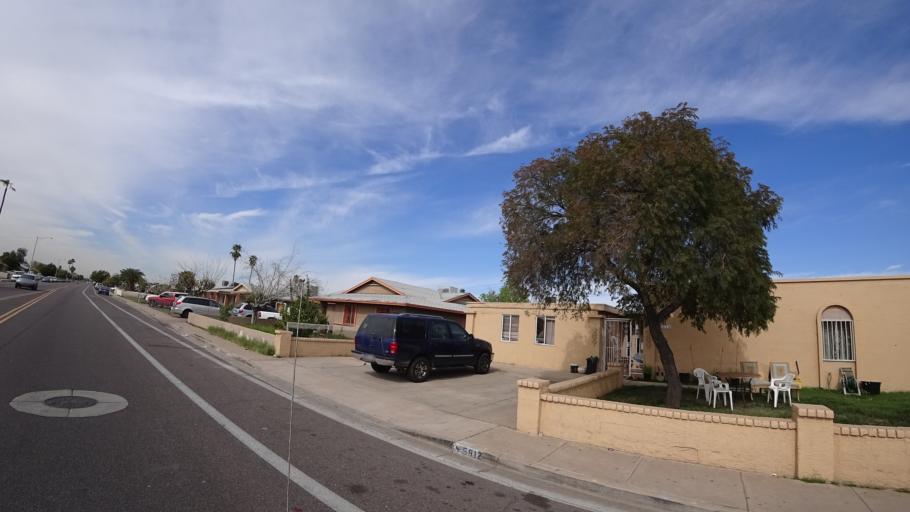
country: US
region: Arizona
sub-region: Maricopa County
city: Glendale
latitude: 33.4878
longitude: -112.1871
